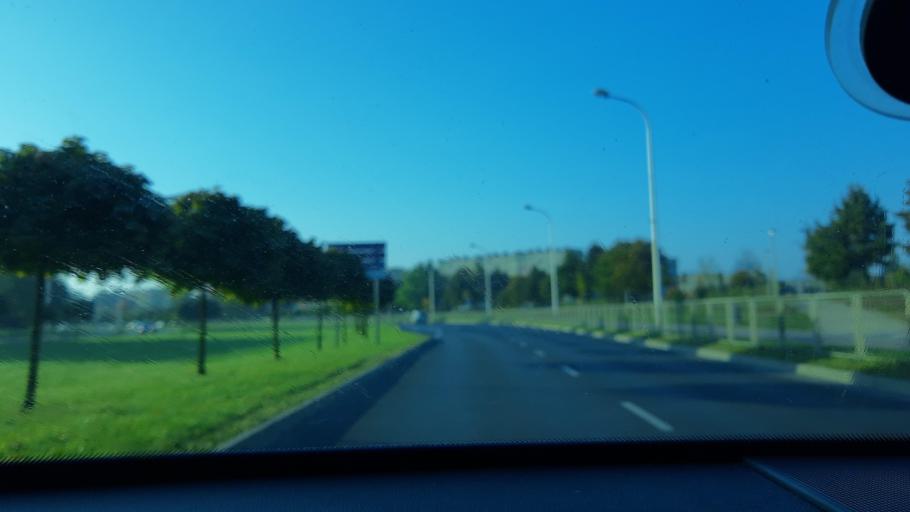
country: PL
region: Lodz Voivodeship
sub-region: Powiat sieradzki
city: Sieradz
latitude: 51.5920
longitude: 18.7146
